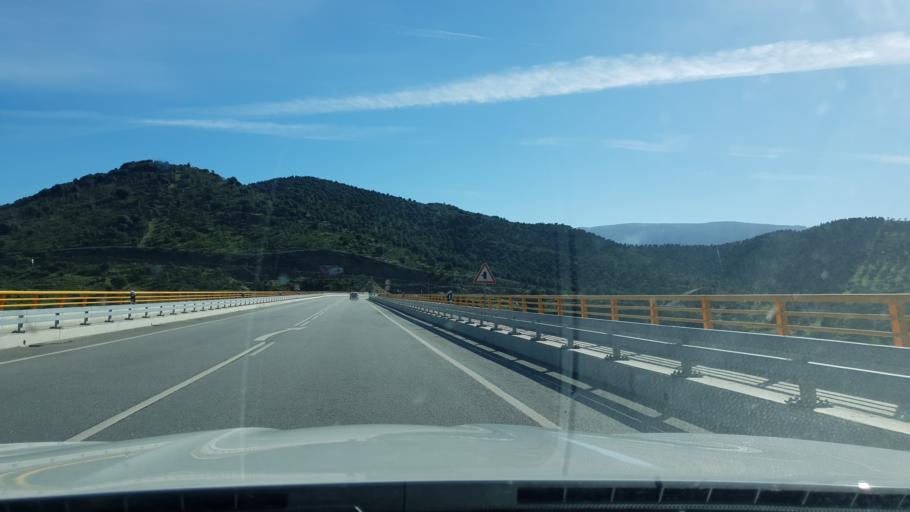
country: PT
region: Braganca
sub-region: Torre de Moncorvo
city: Torre de Moncorvo
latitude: 41.2103
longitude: -7.0846
